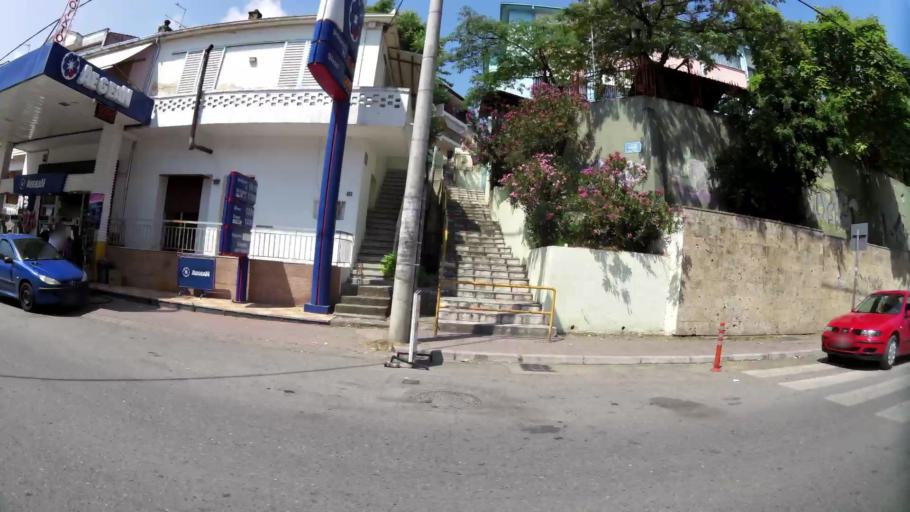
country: GR
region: Central Macedonia
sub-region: Nomos Imathias
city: Veroia
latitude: 40.5193
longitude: 22.2057
